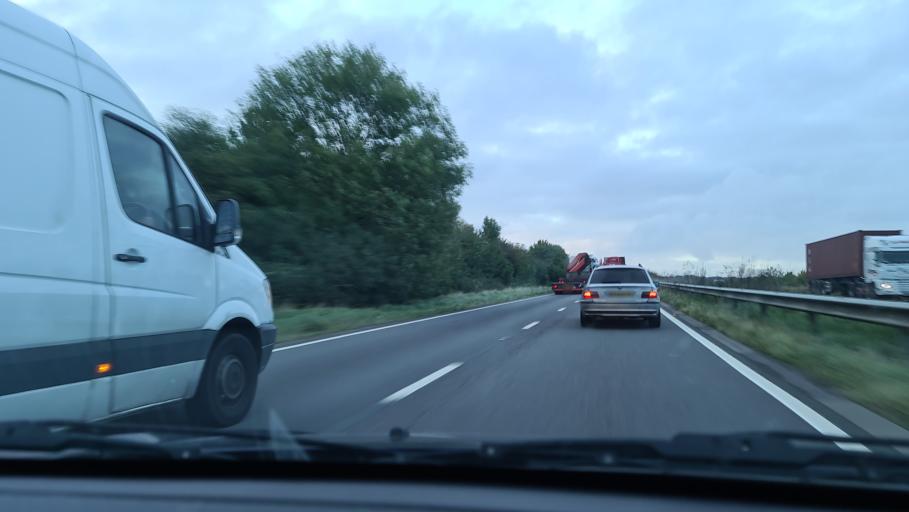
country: GB
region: England
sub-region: Hampshire
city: Overton
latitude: 51.1974
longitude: -1.3367
